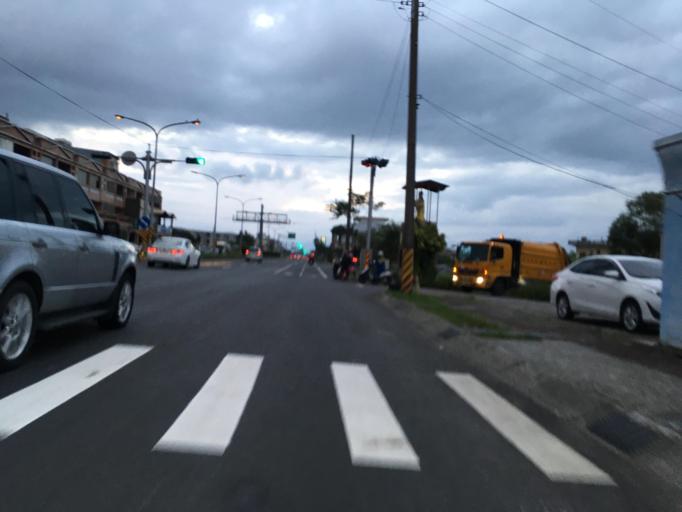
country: TW
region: Taiwan
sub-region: Yilan
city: Yilan
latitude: 24.6220
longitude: 121.8401
